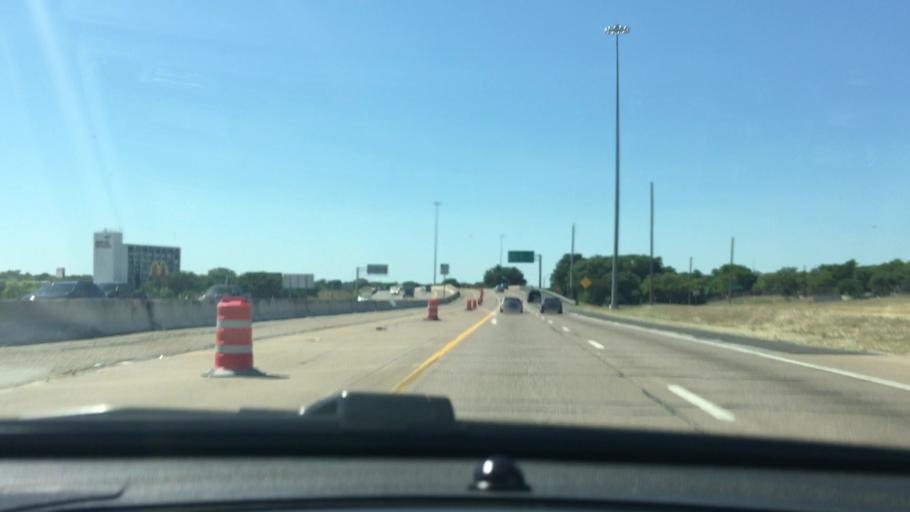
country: US
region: Texas
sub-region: Dallas County
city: Cockrell Hill
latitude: 32.7037
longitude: -96.8258
